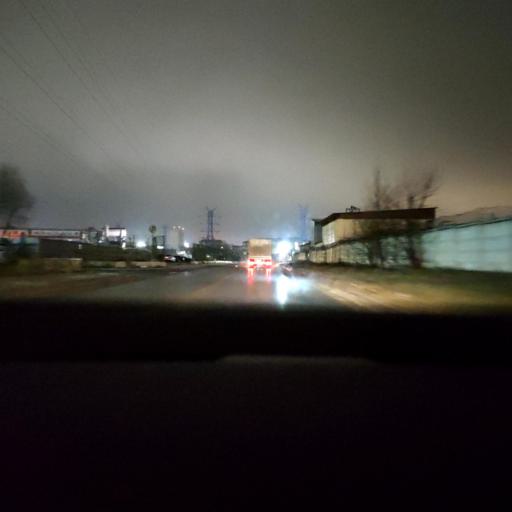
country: RU
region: Moskovskaya
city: Reutov
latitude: 55.7720
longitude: 37.8659
